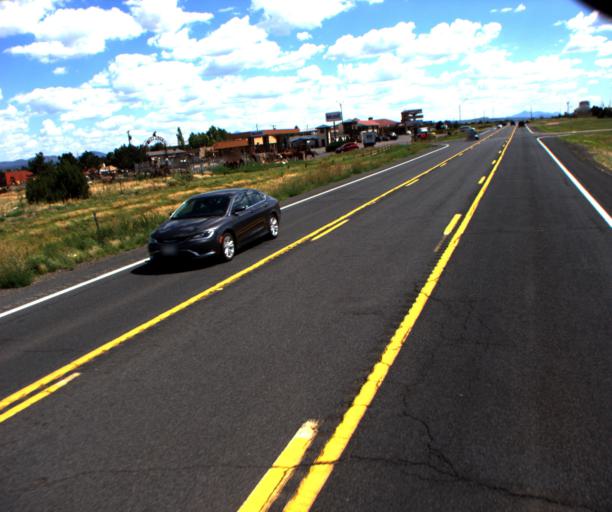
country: US
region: Arizona
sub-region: Coconino County
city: Grand Canyon Village
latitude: 35.6557
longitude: -112.1390
